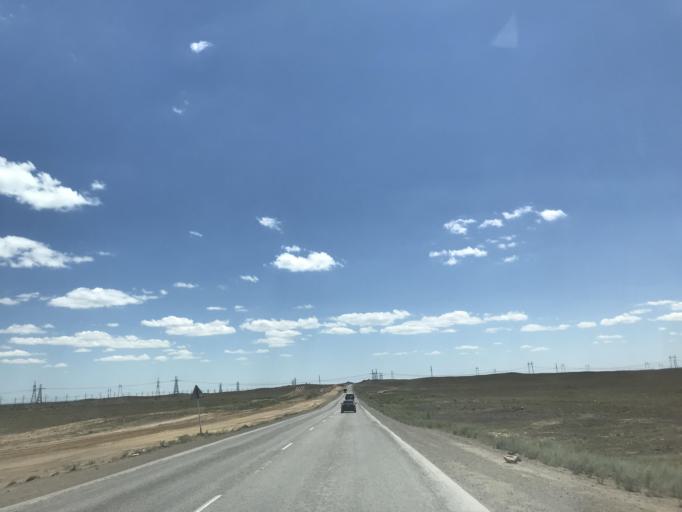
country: KZ
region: Almaty Oblysy
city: Ulken
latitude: 45.1520
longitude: 73.9516
